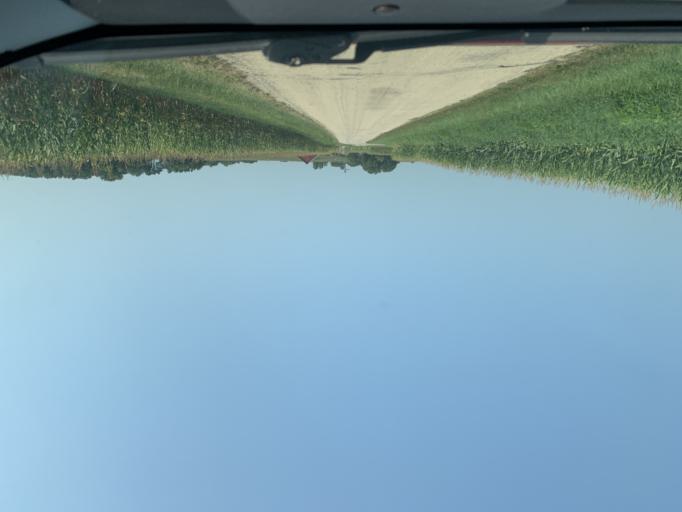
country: US
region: Illinois
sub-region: Whiteside County
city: Morrison
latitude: 41.8683
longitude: -89.8859
